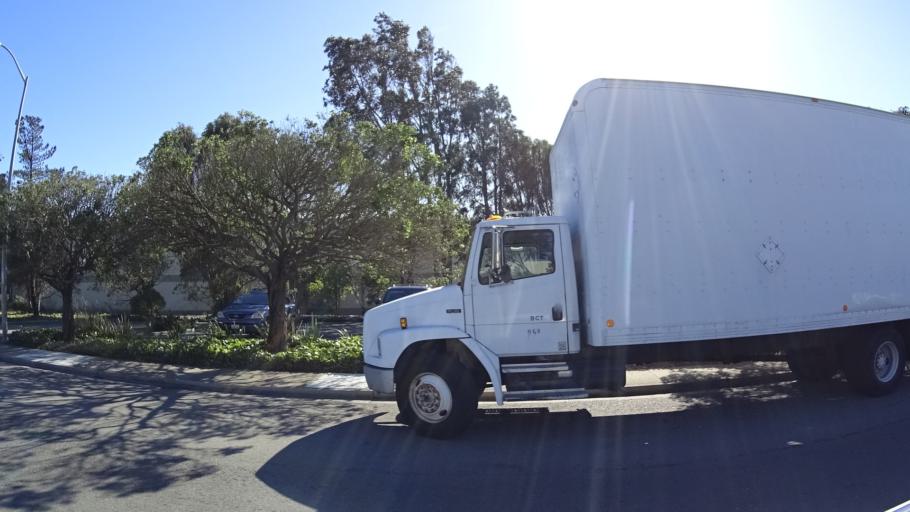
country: US
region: California
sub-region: San Mateo County
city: South San Francisco
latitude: 37.6515
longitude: -122.3879
